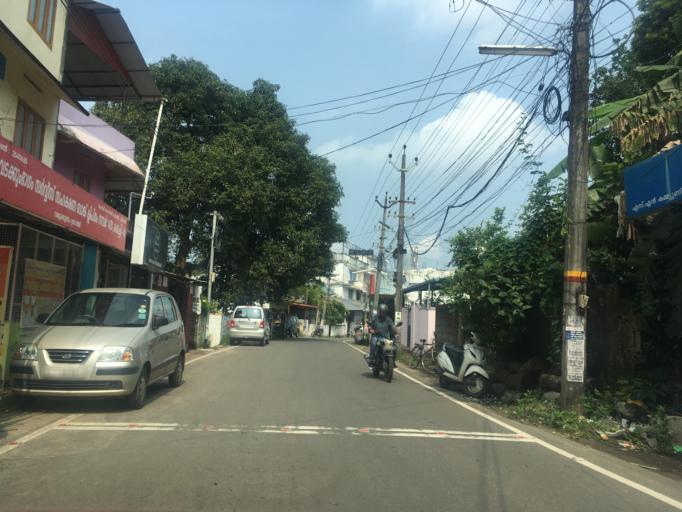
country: IN
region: Kerala
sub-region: Ernakulam
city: Elur
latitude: 10.0410
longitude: 76.3056
